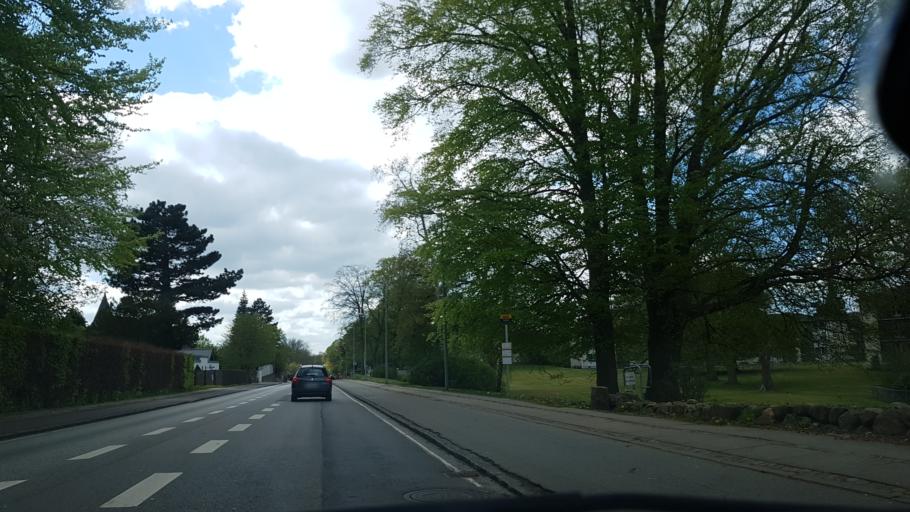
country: DK
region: Capital Region
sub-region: Horsholm Kommune
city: Horsholm
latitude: 55.8815
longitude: 12.5121
